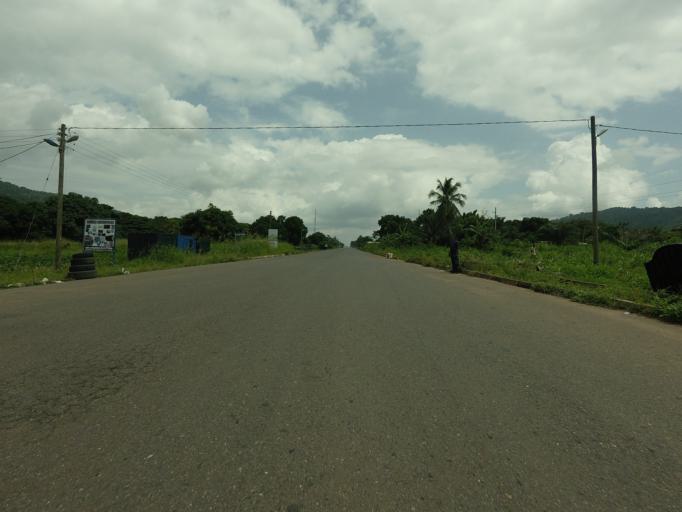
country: GH
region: Volta
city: Ho
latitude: 6.5364
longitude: 0.2320
